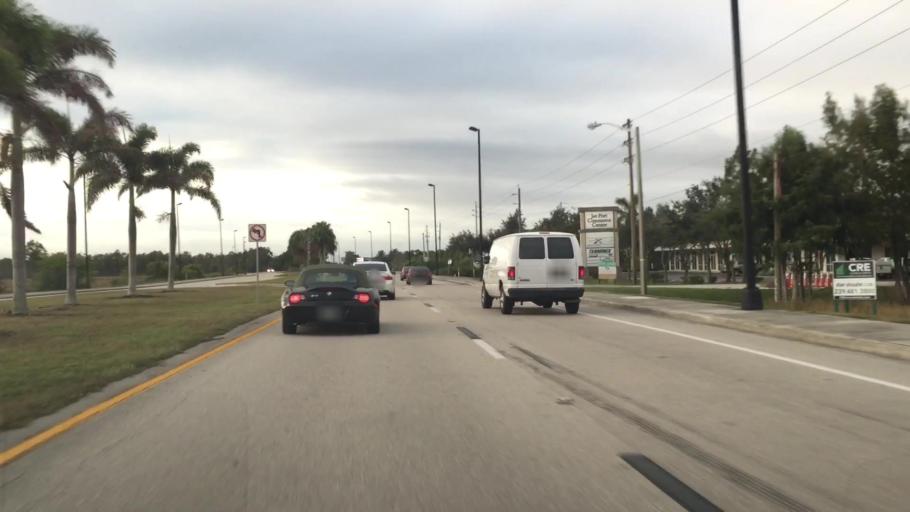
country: US
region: Florida
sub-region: Lee County
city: Gateway
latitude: 26.5417
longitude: -81.7864
